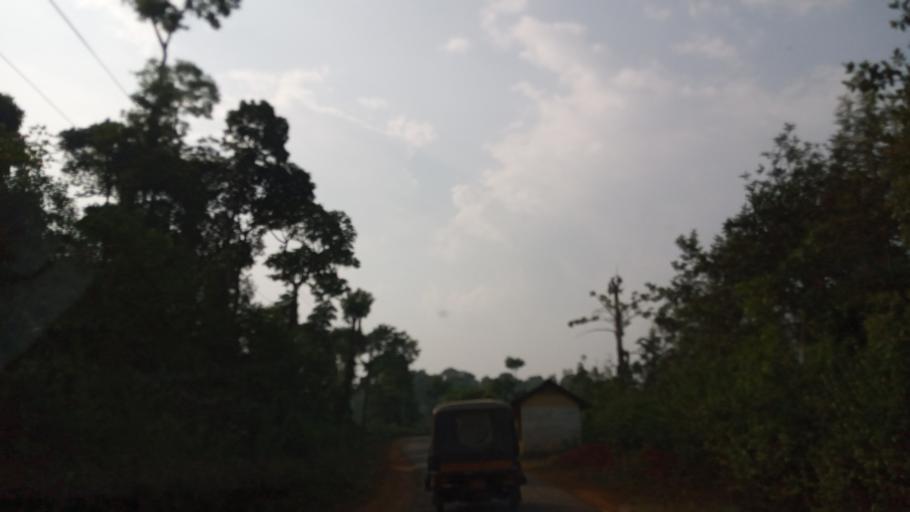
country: IN
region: Karnataka
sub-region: Chikmagalur
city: Mudigere
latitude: 13.0570
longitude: 75.6547
